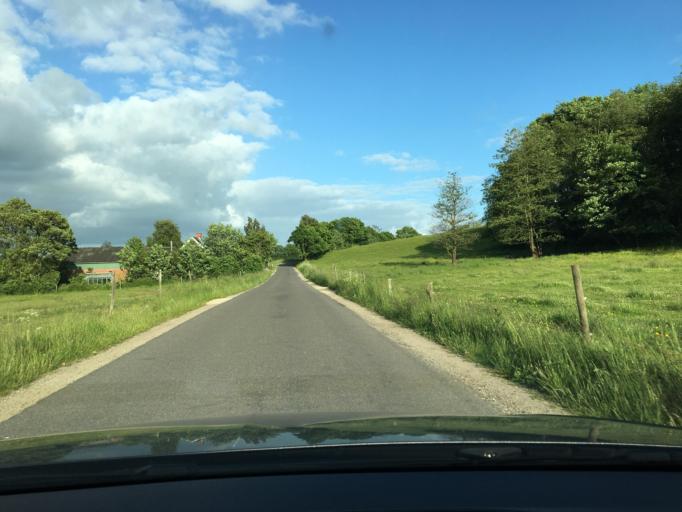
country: DK
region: Central Jutland
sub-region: Favrskov Kommune
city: Hinnerup
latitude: 56.3037
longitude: 10.1000
